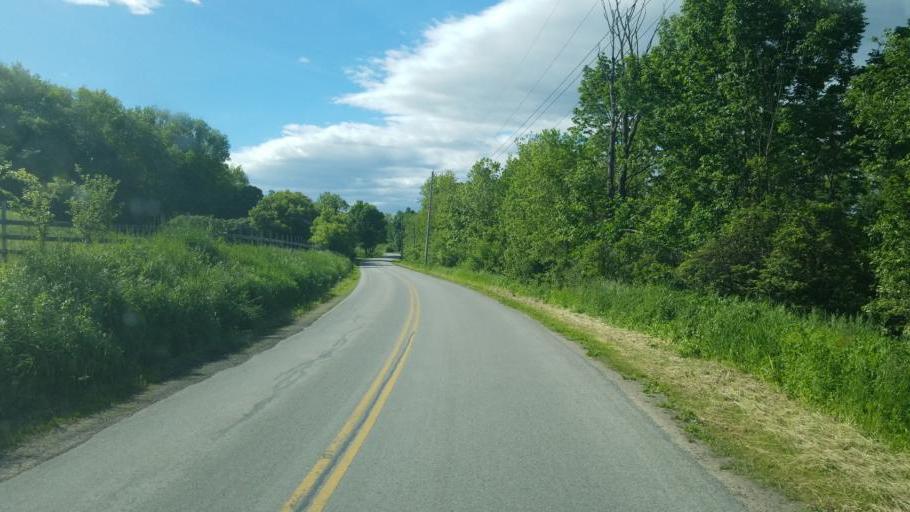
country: US
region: New York
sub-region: Montgomery County
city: Saint Johnsville
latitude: 42.9715
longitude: -74.6501
